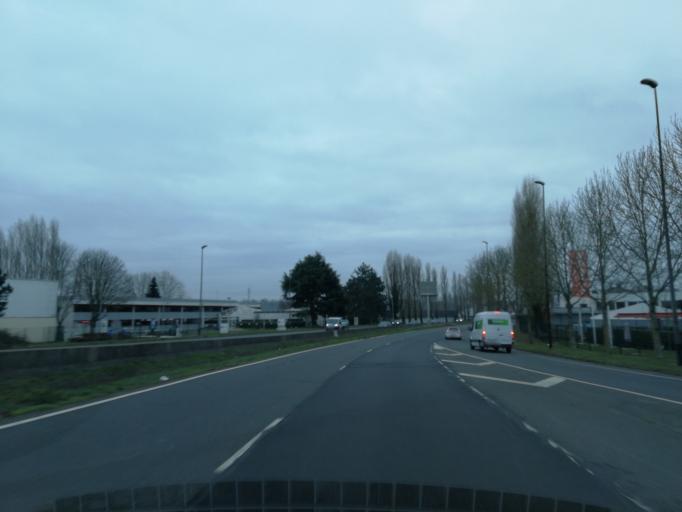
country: FR
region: Ile-de-France
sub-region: Departement de l'Essonne
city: Orsay
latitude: 48.6828
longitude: 2.2045
